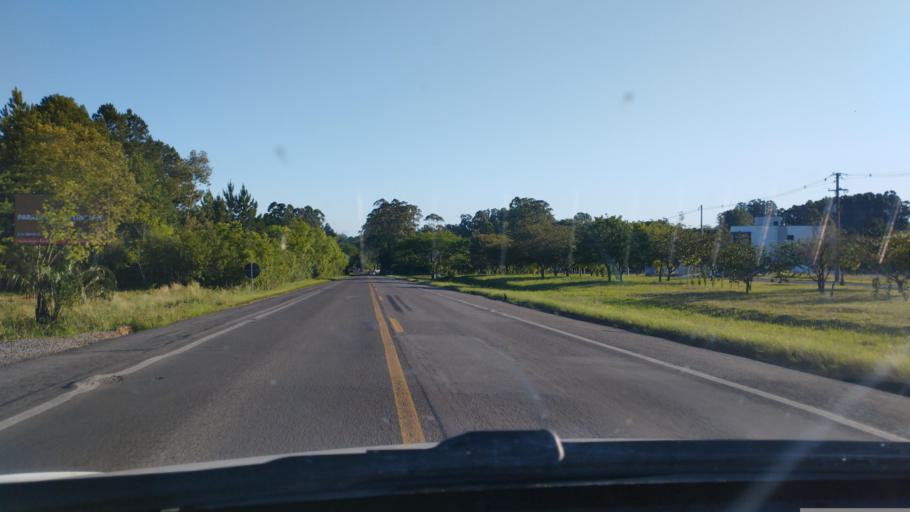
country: BR
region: Rio Grande do Sul
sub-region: Santa Maria
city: Santa Maria
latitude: -29.5936
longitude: -53.7664
